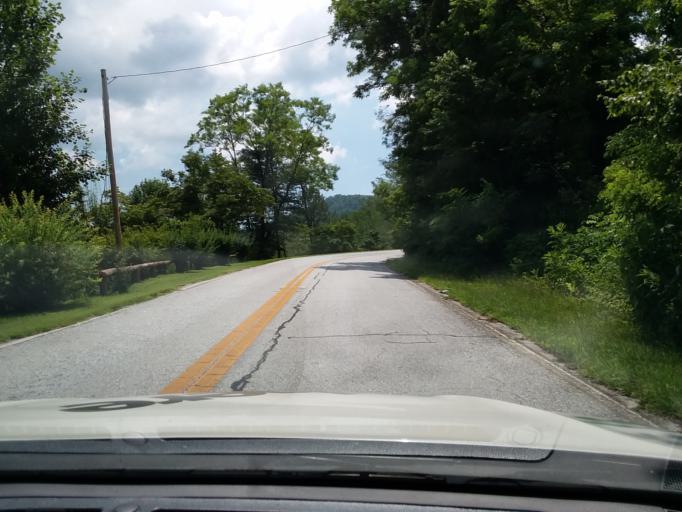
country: US
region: Georgia
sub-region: Rabun County
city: Mountain City
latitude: 34.9816
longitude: -83.1871
